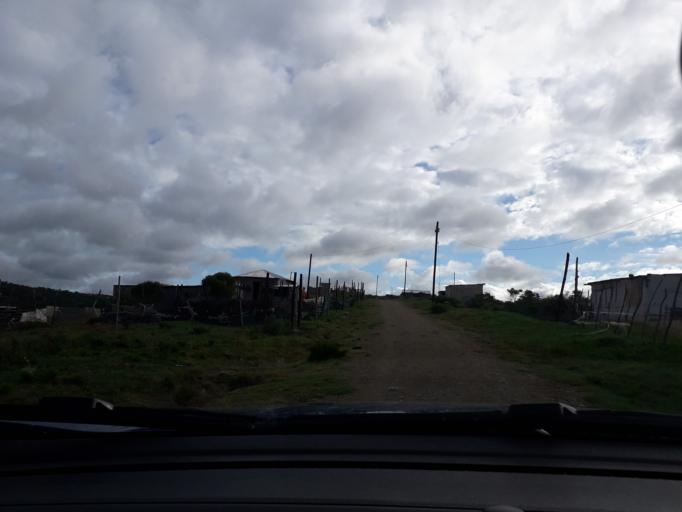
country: ZA
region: Eastern Cape
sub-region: Buffalo City Metropolitan Municipality
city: East London
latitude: -32.8036
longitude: 27.9674
